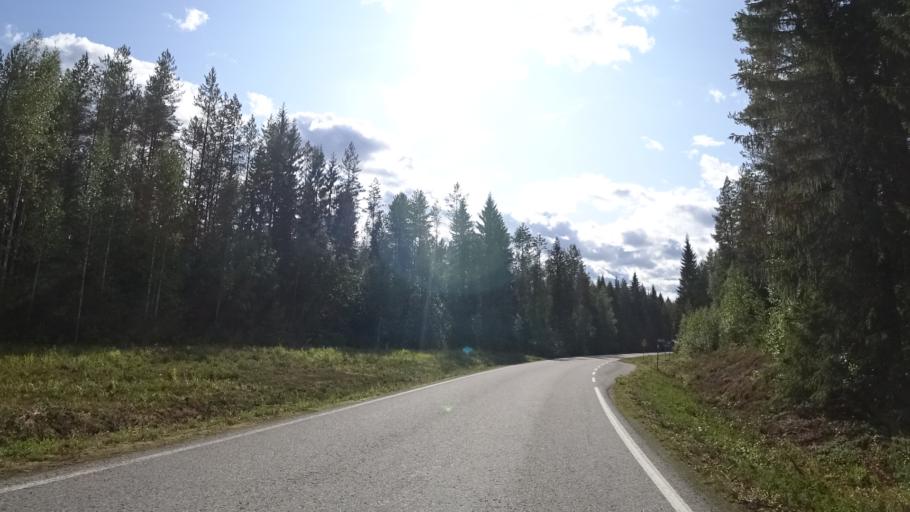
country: RU
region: Republic of Karelia
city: Vyartsilya
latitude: 62.2498
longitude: 30.7311
